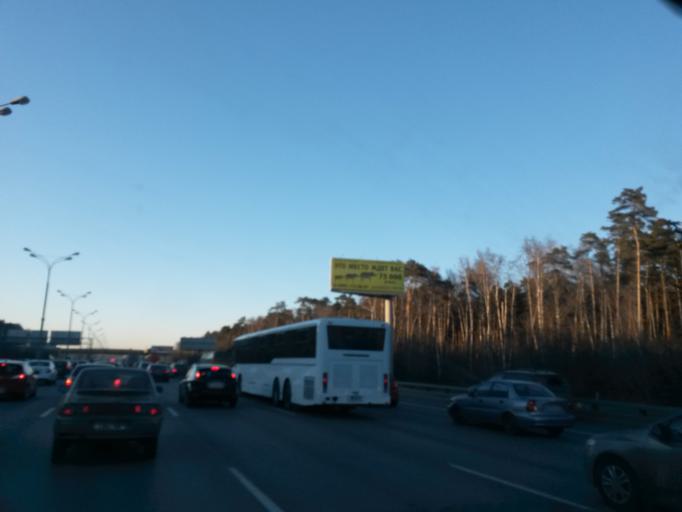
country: RU
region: Moskovskaya
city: Kotel'niki
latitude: 55.6641
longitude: 37.8392
